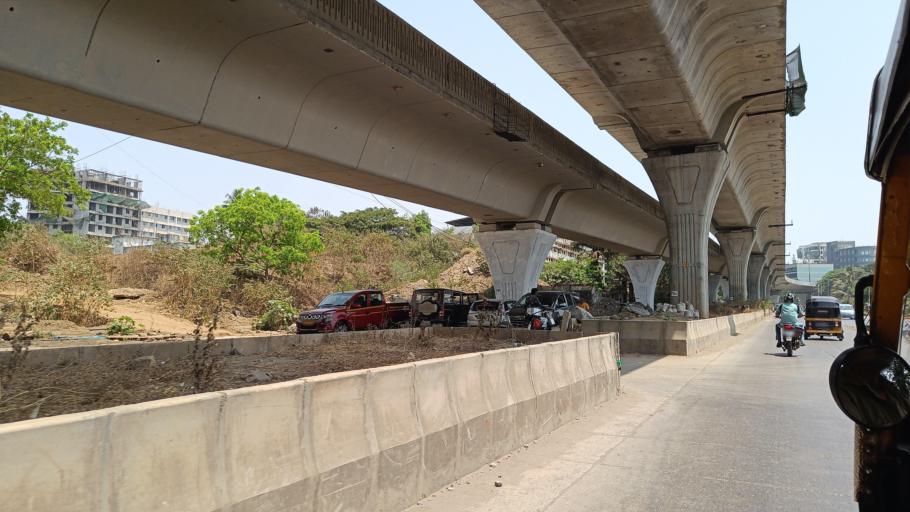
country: IN
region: Maharashtra
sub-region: Mumbai Suburban
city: Mumbai
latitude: 19.0754
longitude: 72.8573
